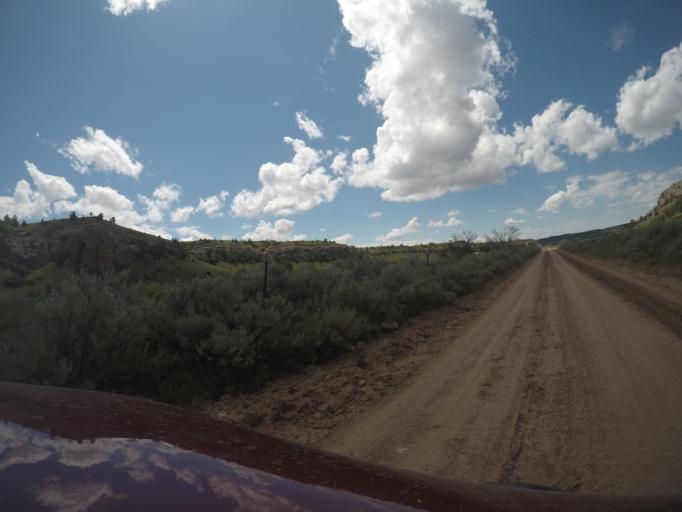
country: US
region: Montana
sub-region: Yellowstone County
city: Laurel
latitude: 45.2372
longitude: -108.6245
